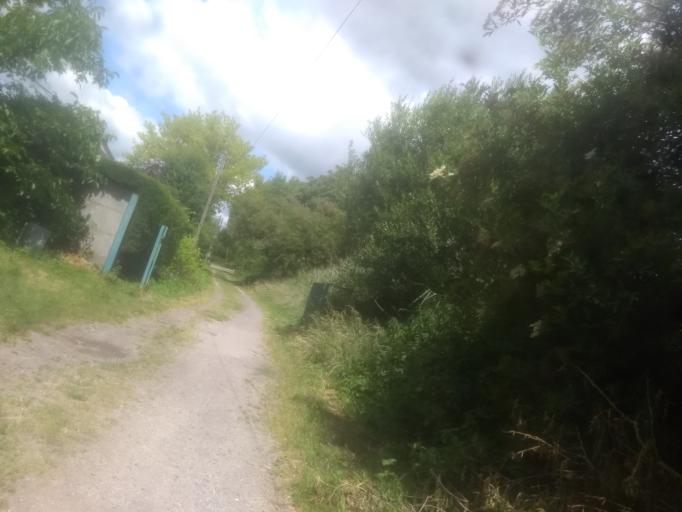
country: FR
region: Nord-Pas-de-Calais
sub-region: Departement du Pas-de-Calais
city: Anzin-Saint-Aubin
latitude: 50.3050
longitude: 2.7539
